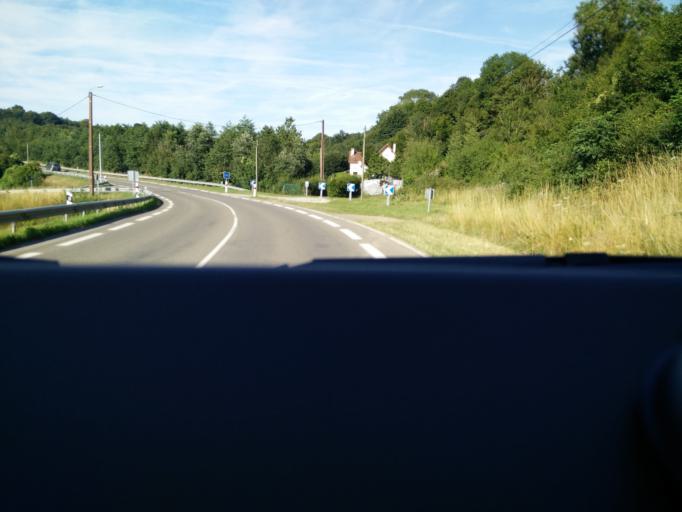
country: FR
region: Nord-Pas-de-Calais
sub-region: Departement du Nord
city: Trelon
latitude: 50.1250
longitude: 4.0823
